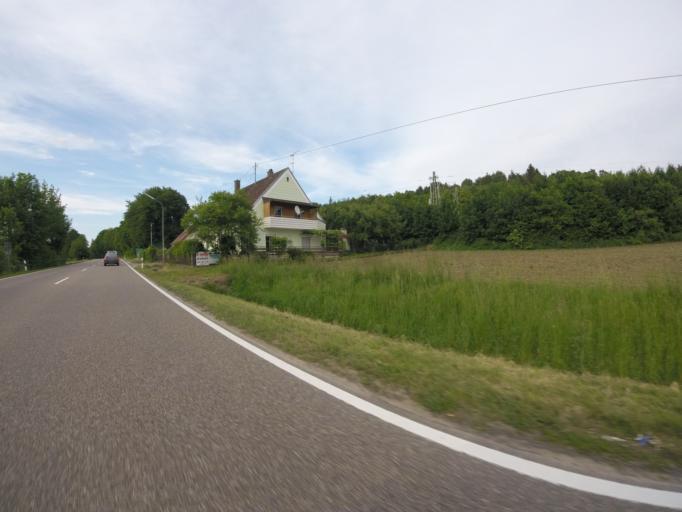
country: DE
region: Bavaria
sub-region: Upper Bavaria
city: Ilmmunster
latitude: 48.4793
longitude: 11.5097
